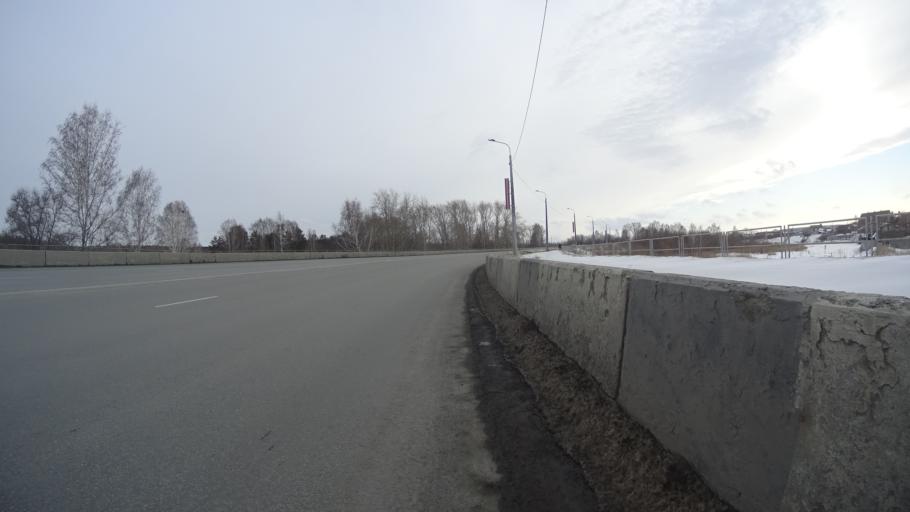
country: RU
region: Chelyabinsk
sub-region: Gorod Chelyabinsk
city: Chelyabinsk
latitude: 55.1528
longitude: 61.3196
